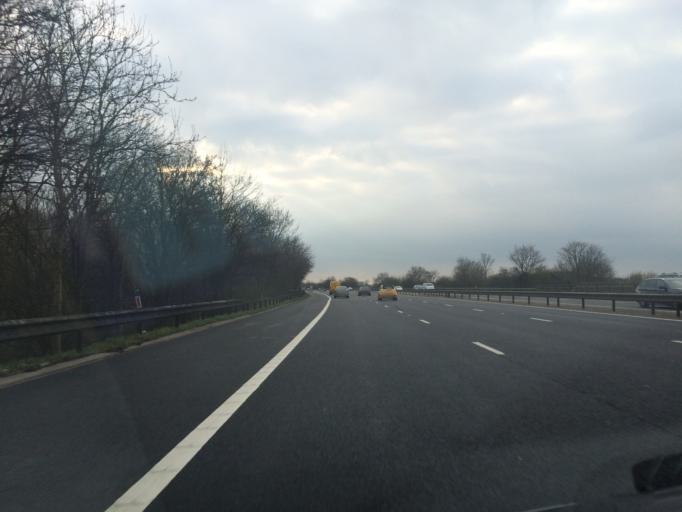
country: GB
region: England
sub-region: West Berkshire
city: Hermitage
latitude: 51.4650
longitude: -1.2643
